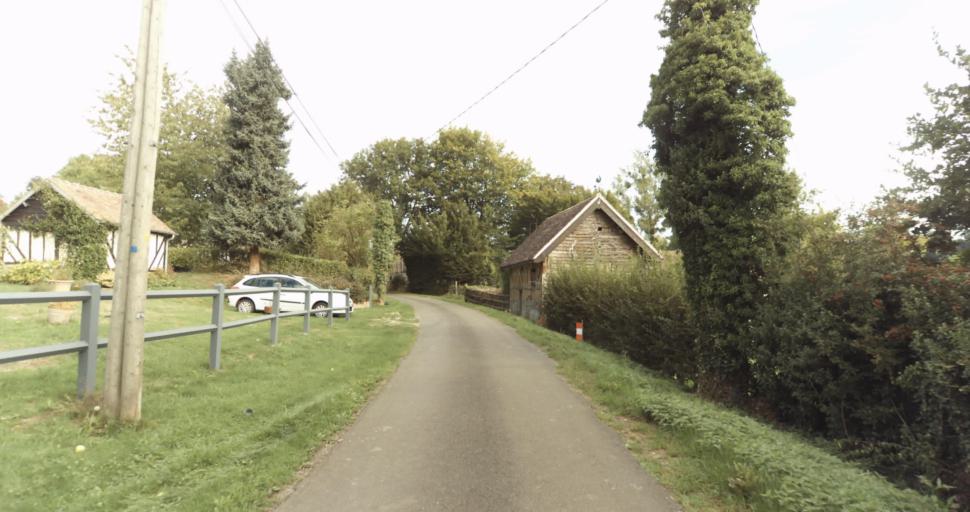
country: FR
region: Lower Normandy
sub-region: Departement de l'Orne
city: Vimoutiers
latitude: 48.8488
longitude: 0.2238
